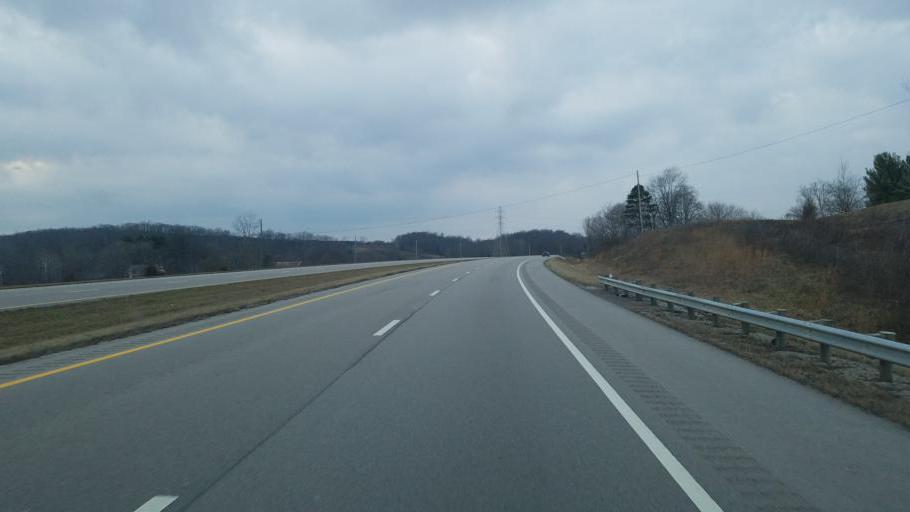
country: US
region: Ohio
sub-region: Jackson County
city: Oak Hill
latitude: 38.8852
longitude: -82.4232
